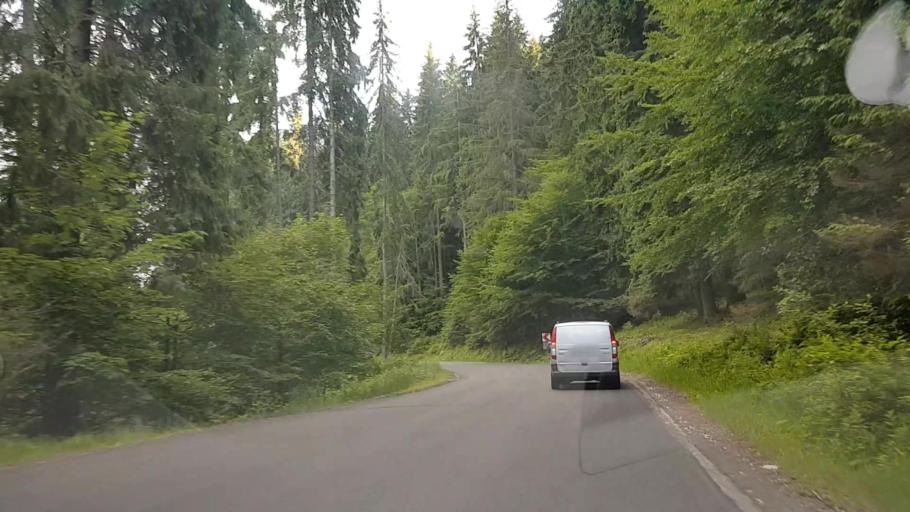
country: RO
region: Harghita
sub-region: Comuna Varsag
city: Varsag
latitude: 46.6683
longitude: 25.3189
